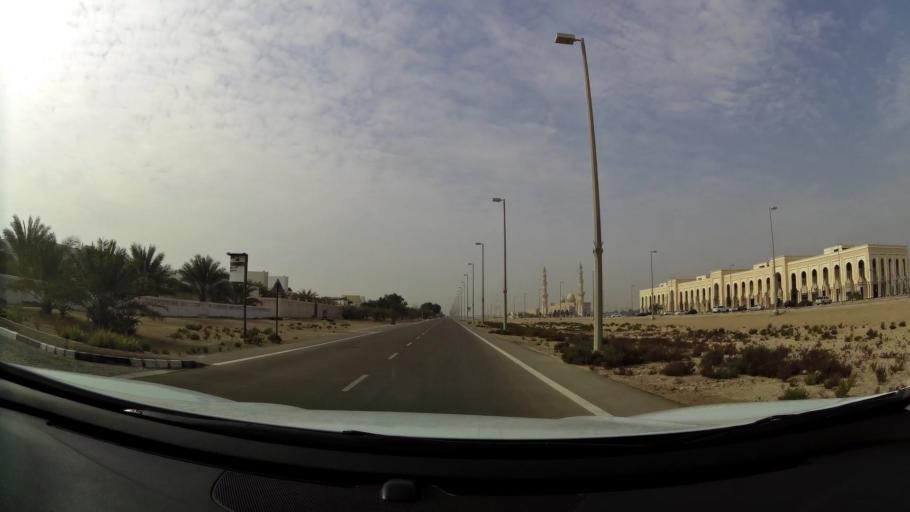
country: AE
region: Abu Dhabi
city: Abu Dhabi
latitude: 24.6671
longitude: 54.7630
